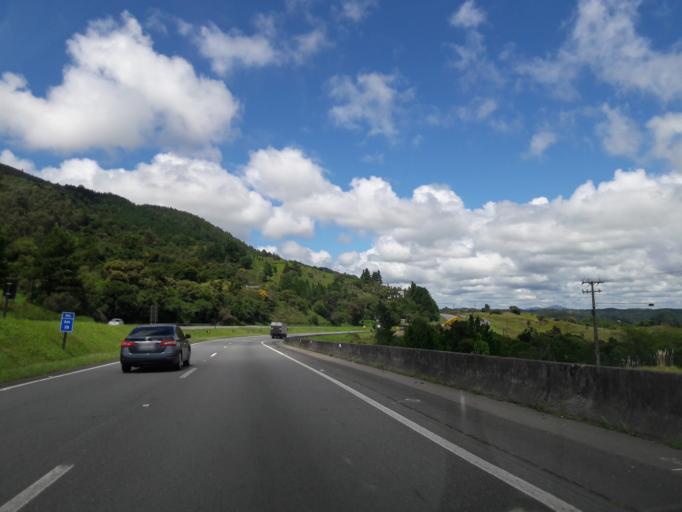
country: BR
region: Parana
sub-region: Campina Grande Do Sul
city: Campina Grande do Sul
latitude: -25.1499
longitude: -48.8594
